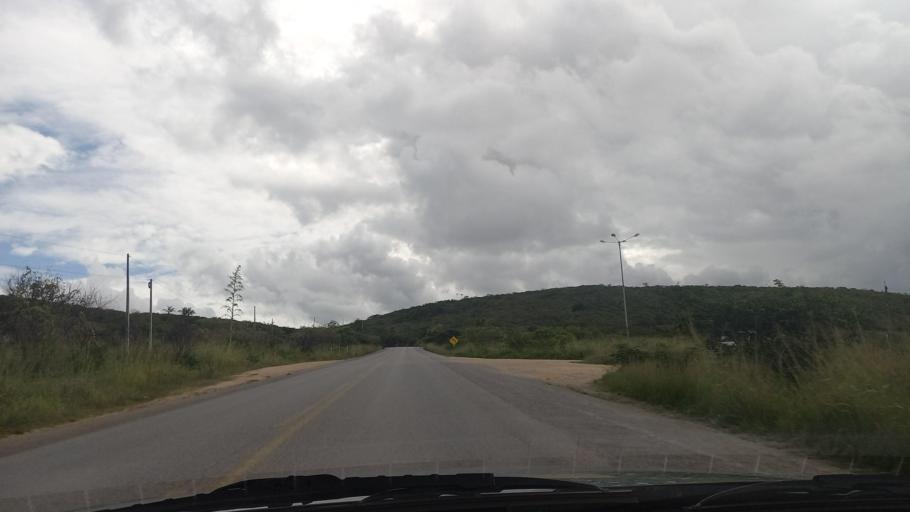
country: BR
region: Pernambuco
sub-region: Lajedo
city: Lajedo
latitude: -8.6732
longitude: -36.3959
